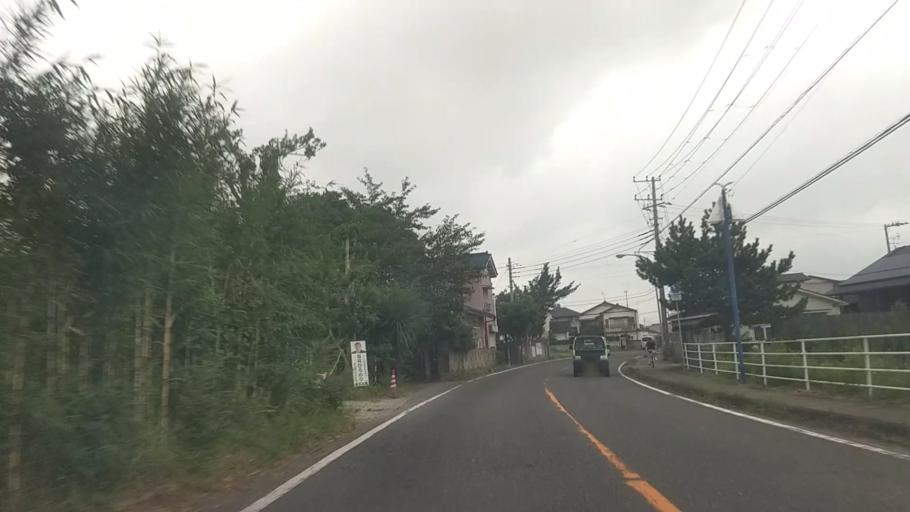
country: JP
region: Chiba
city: Kawaguchi
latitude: 35.1093
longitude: 140.0840
